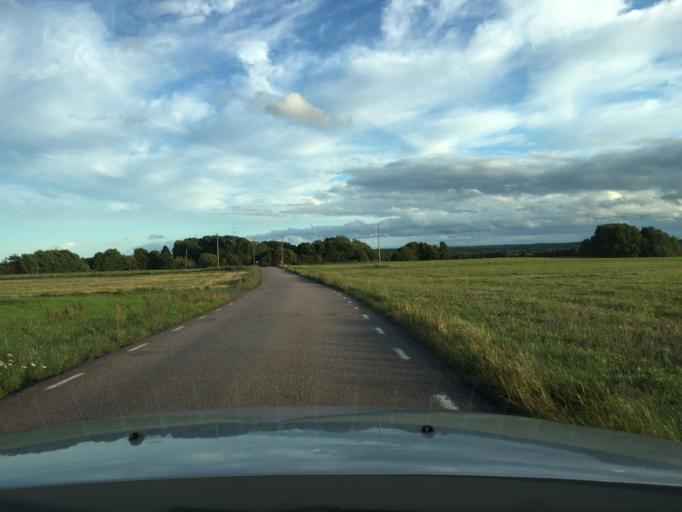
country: SE
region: Skane
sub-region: Hassleholms Kommun
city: Sosdala
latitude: 56.0250
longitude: 13.7560
